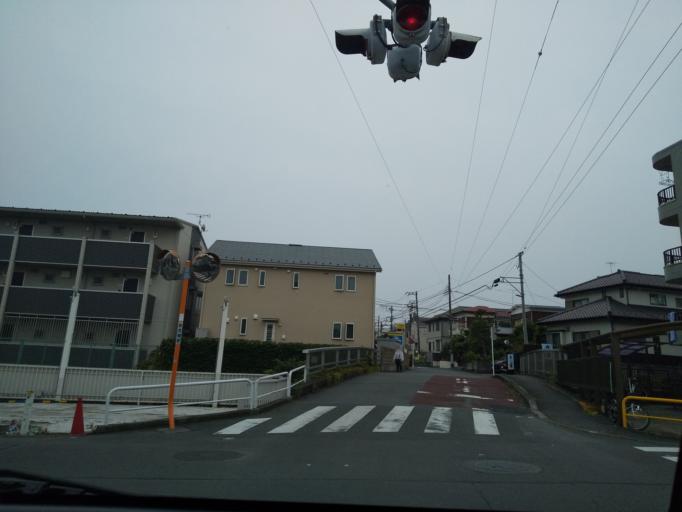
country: JP
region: Kanagawa
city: Zama
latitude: 35.5000
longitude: 139.4049
